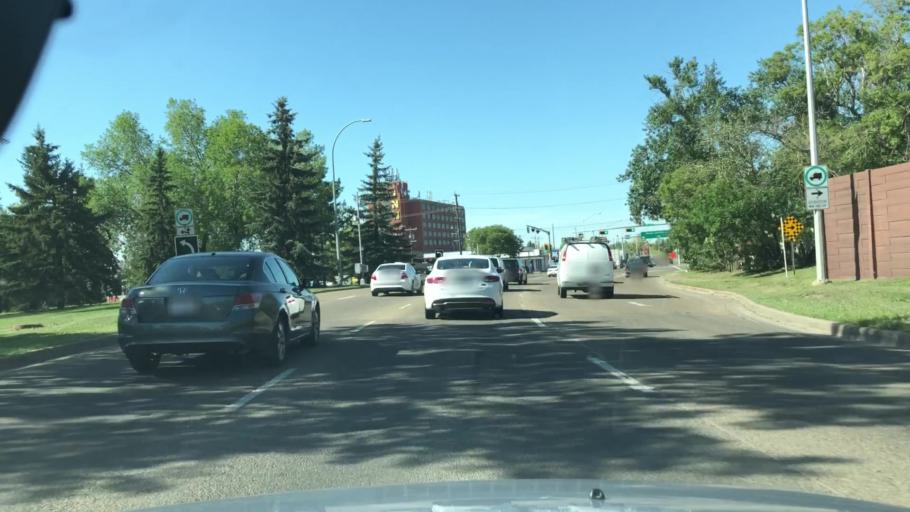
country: CA
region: Alberta
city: Edmonton
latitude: 53.5694
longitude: -113.4520
